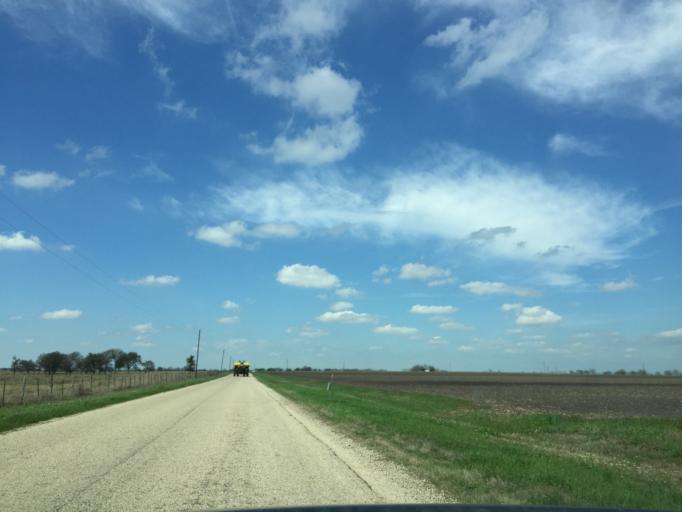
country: US
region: Texas
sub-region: Milam County
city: Thorndale
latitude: 30.5442
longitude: -97.2714
